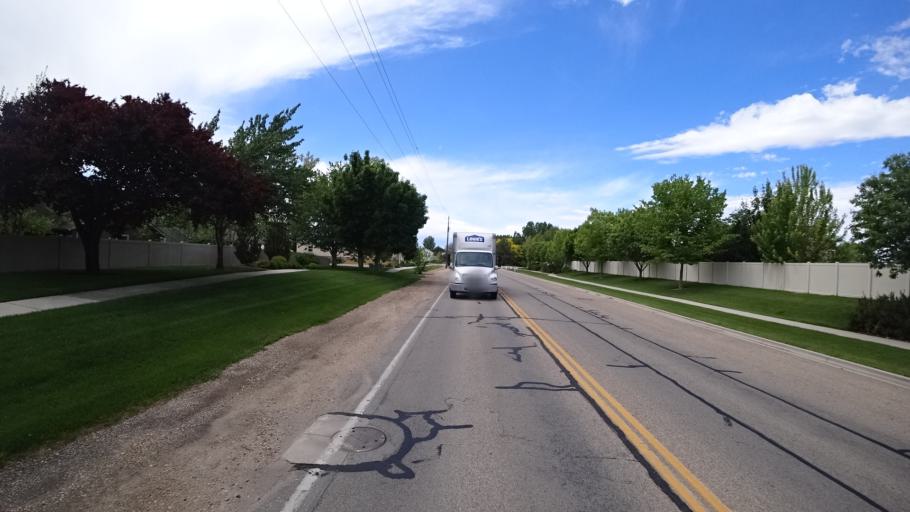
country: US
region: Idaho
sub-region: Ada County
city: Meridian
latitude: 43.5756
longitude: -116.3789
